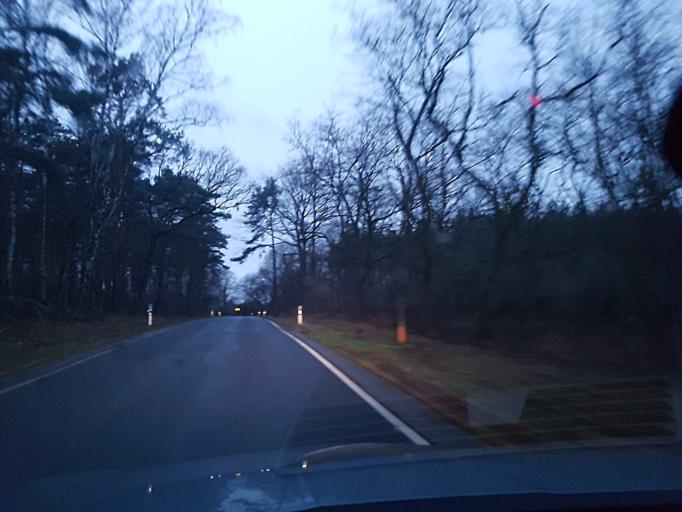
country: DE
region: Brandenburg
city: Bad Liebenwerda
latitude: 51.5466
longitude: 13.4280
